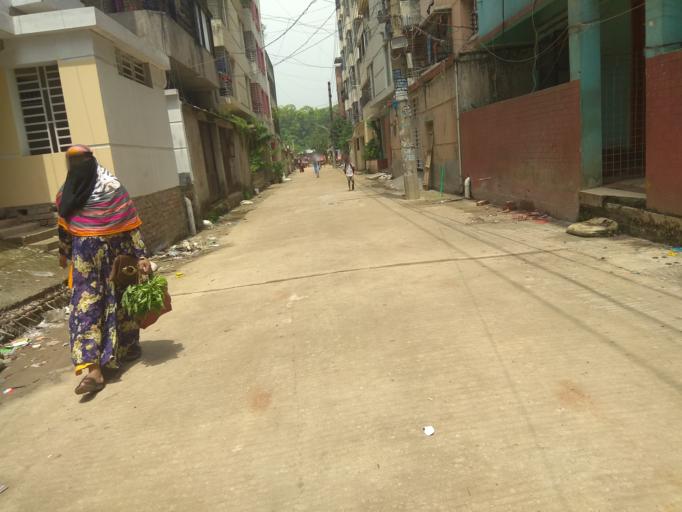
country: BD
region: Dhaka
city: Tungi
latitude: 23.8164
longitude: 90.3535
